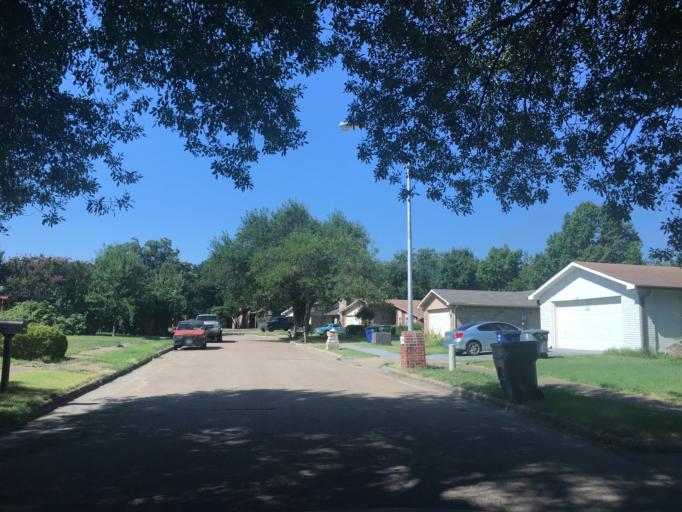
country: US
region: Texas
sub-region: Dallas County
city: Garland
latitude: 32.8524
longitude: -96.6577
